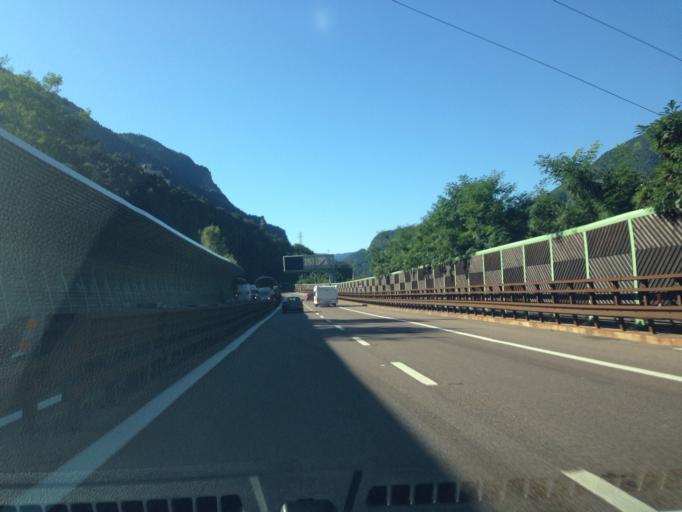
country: IT
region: Trentino-Alto Adige
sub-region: Bolzano
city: Ponte Gardena
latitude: 46.6023
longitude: 11.5344
